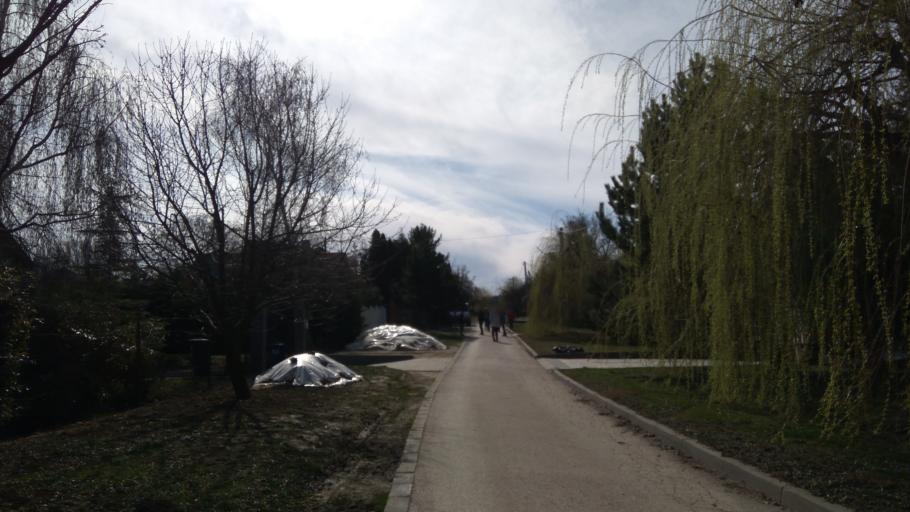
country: HU
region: Pest
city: Urom
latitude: 47.6147
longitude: 19.0186
